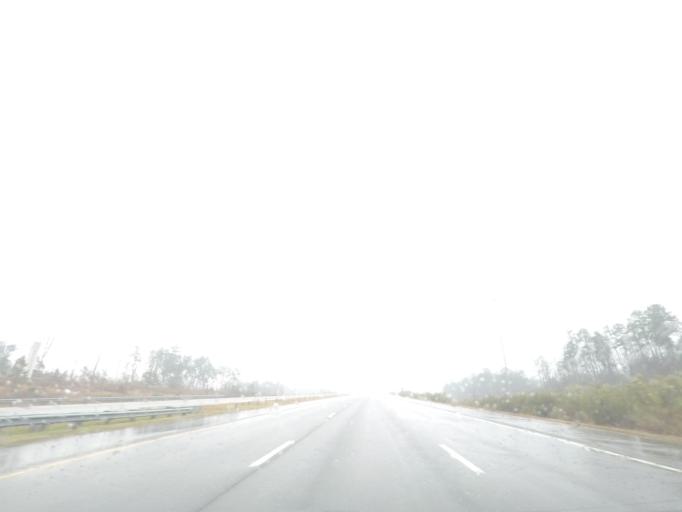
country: US
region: North Carolina
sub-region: Wake County
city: Morrisville
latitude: 35.8764
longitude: -78.8668
